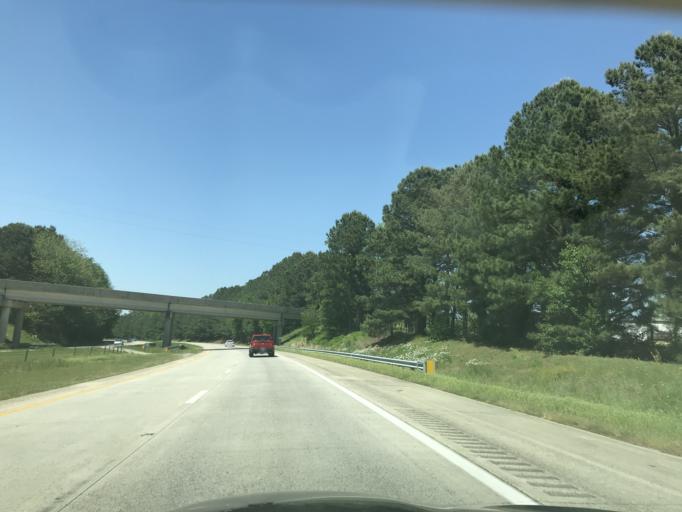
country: US
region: North Carolina
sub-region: Johnston County
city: Benson
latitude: 35.4490
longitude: -78.5332
